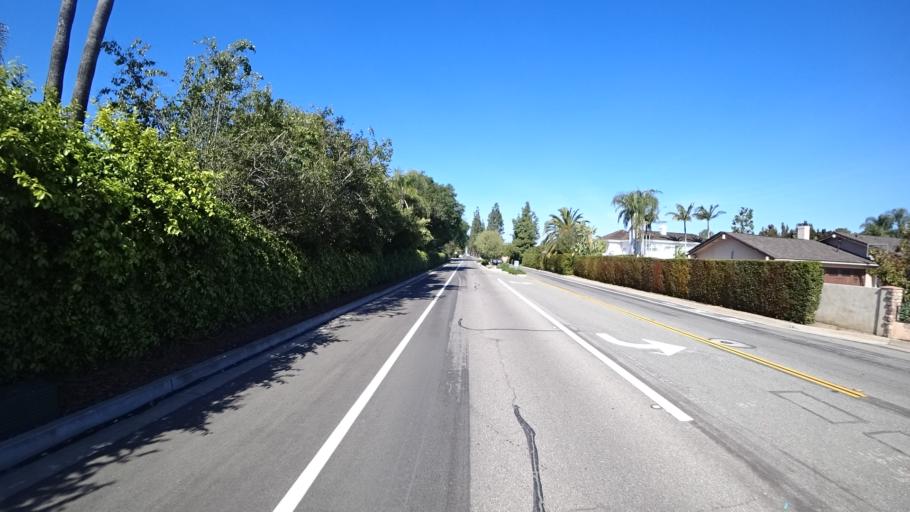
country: US
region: California
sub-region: Orange County
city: Villa Park
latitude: 33.8180
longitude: -117.8075
